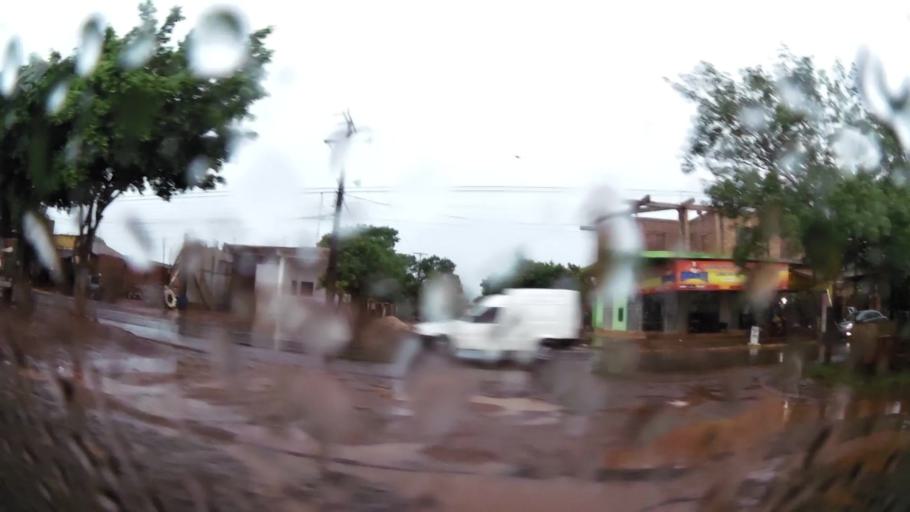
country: PY
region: Alto Parana
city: Presidente Franco
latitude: -25.5188
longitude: -54.6748
